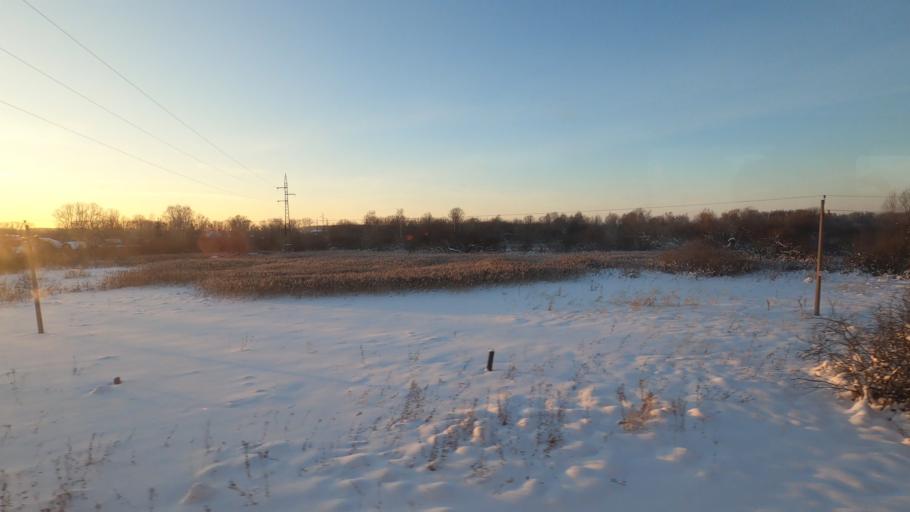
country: RU
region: Moskovskaya
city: Dmitrov
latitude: 56.3576
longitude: 37.5209
